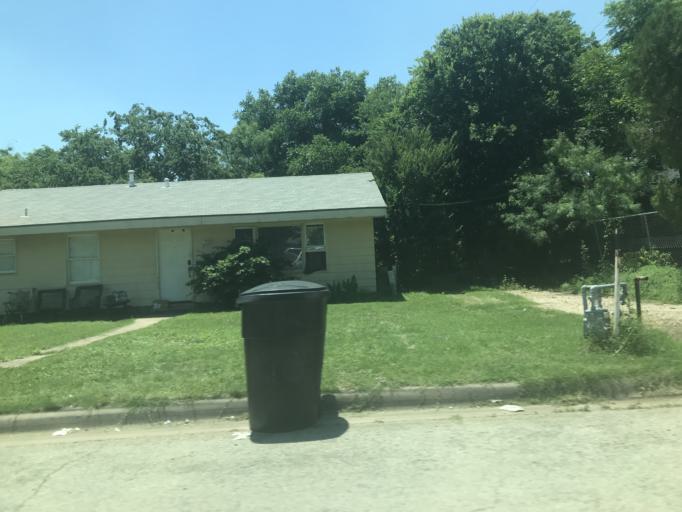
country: US
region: Texas
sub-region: Taylor County
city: Abilene
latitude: 32.4632
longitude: -99.7123
